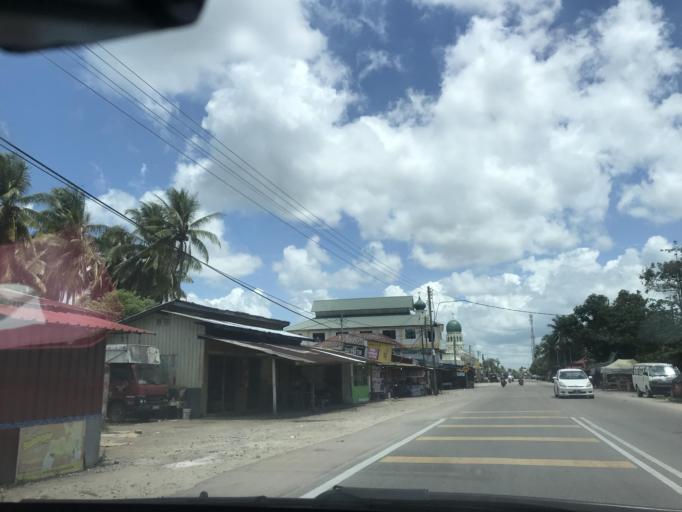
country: MY
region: Kelantan
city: Tumpat
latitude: 6.2212
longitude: 102.1106
